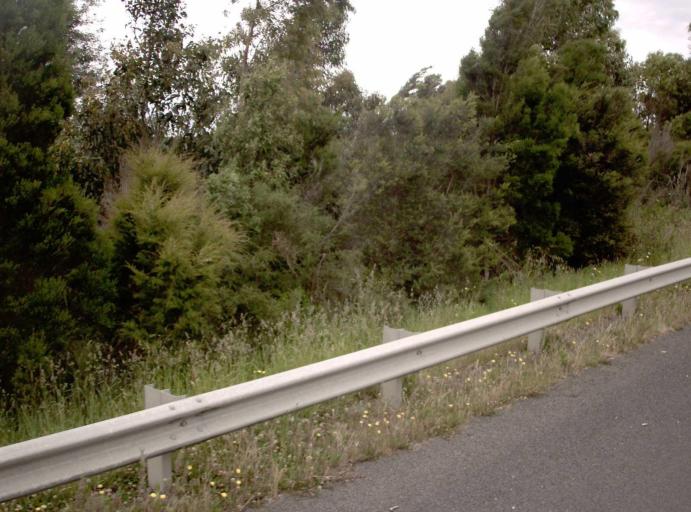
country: AU
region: Victoria
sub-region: Bass Coast
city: North Wonthaggi
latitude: -38.4136
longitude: 145.7769
